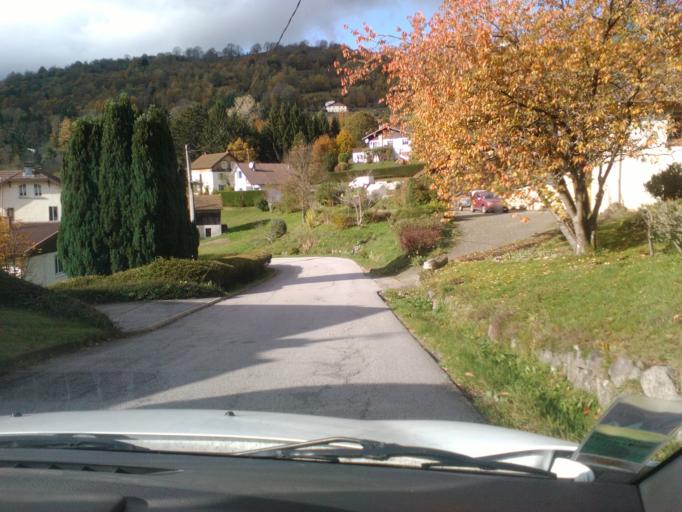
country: FR
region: Lorraine
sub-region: Departement des Vosges
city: Saulxures-sur-Moselotte
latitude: 47.9547
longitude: 6.7832
